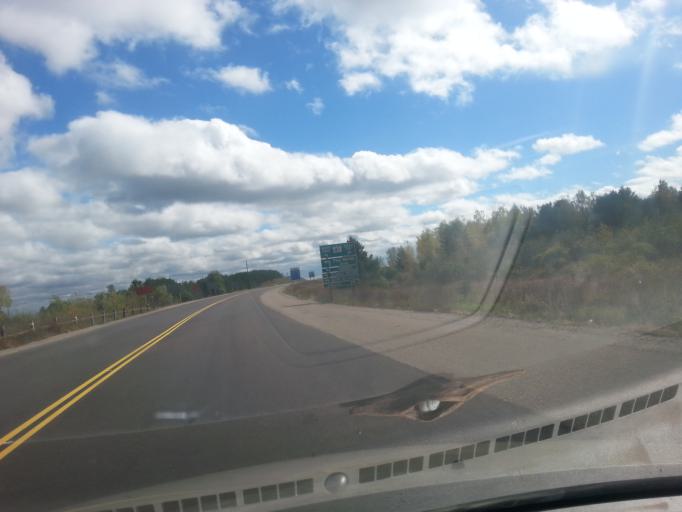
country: CA
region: Ontario
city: Pembroke
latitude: 45.7995
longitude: -77.1251
